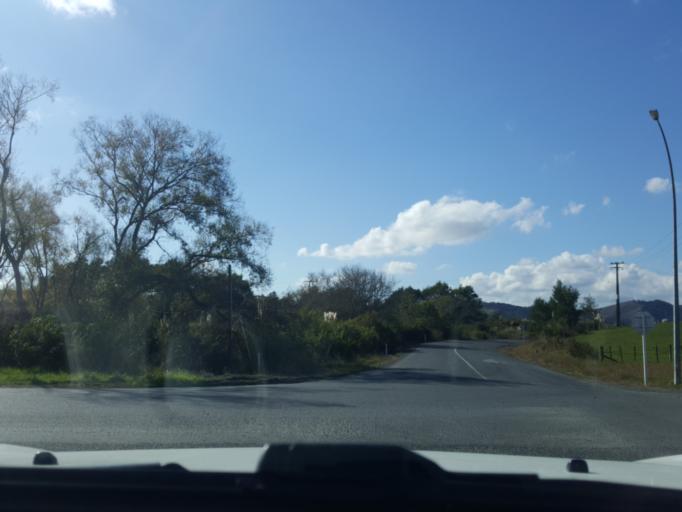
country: NZ
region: Waikato
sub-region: Waikato District
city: Ngaruawahia
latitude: -37.5401
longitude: 175.1738
